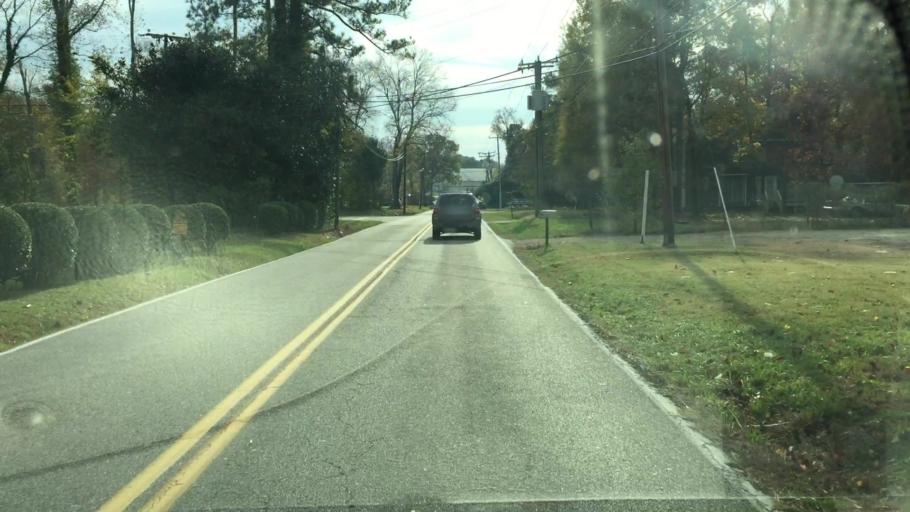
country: US
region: Virginia
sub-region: Chesterfield County
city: Bon Air
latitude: 37.5107
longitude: -77.5794
